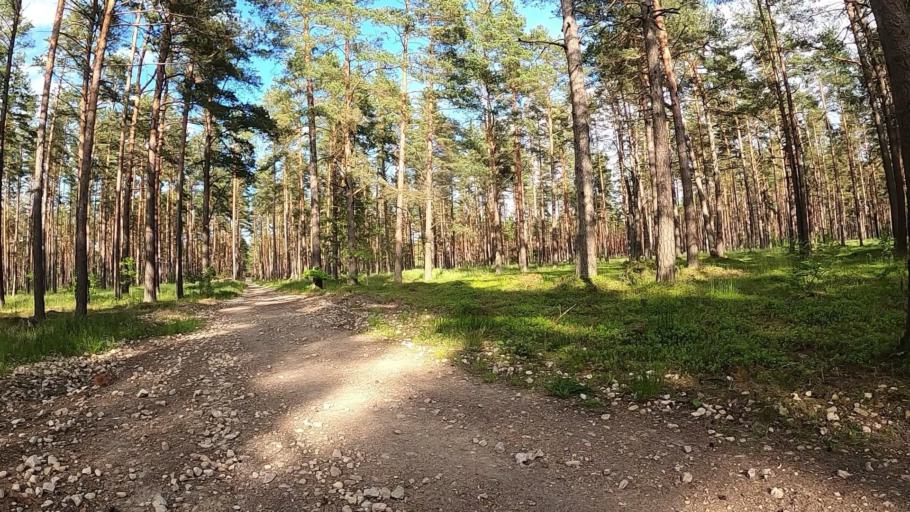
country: LV
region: Riga
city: Jaunciems
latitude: 57.0519
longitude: 24.1167
